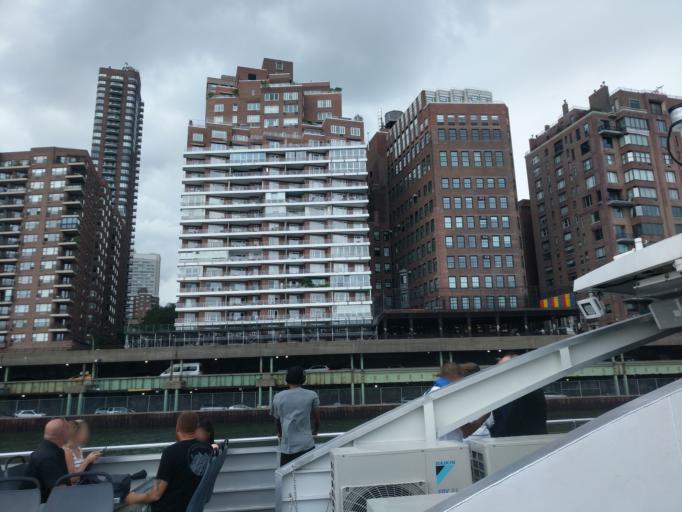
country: US
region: New York
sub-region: New York County
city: Manhattan
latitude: 40.7717
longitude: -73.9447
